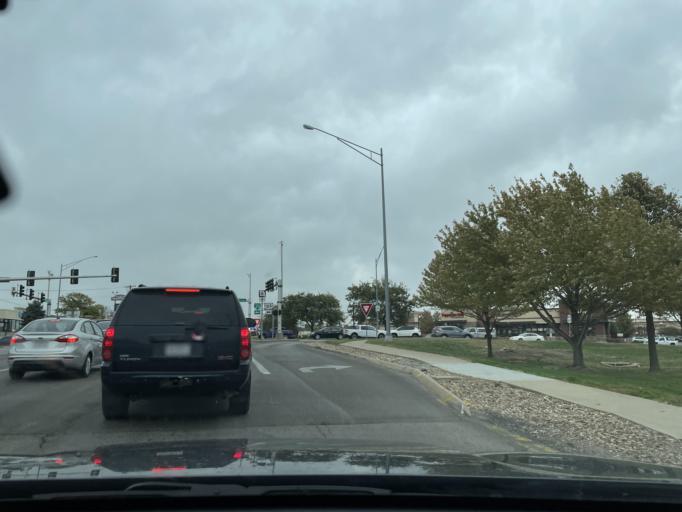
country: US
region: Missouri
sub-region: Buchanan County
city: Saint Joseph
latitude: 39.7769
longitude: -94.8039
